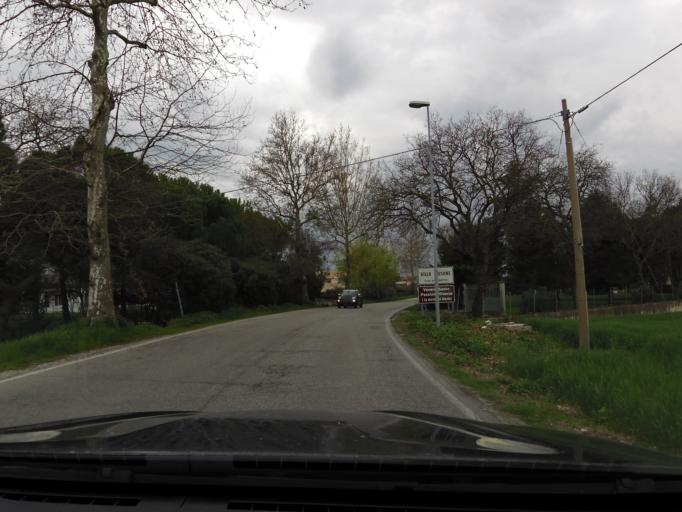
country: IT
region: The Marches
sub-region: Provincia di Ancona
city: Villa Musone
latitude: 43.4461
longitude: 13.6113
